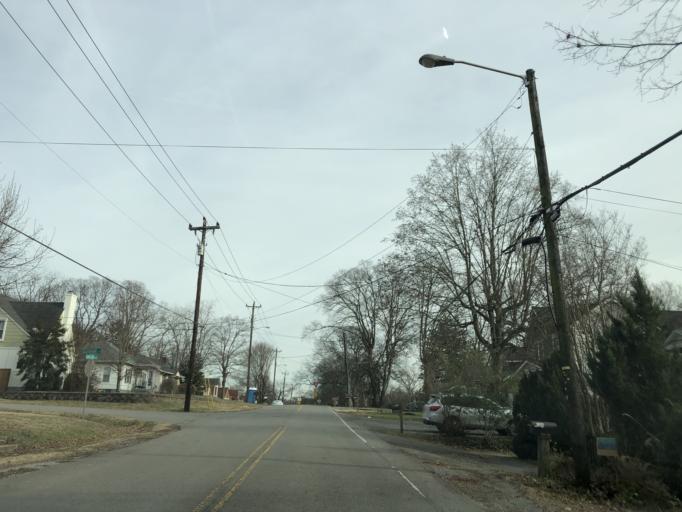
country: US
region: Tennessee
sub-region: Davidson County
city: Nashville
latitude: 36.2080
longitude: -86.7294
